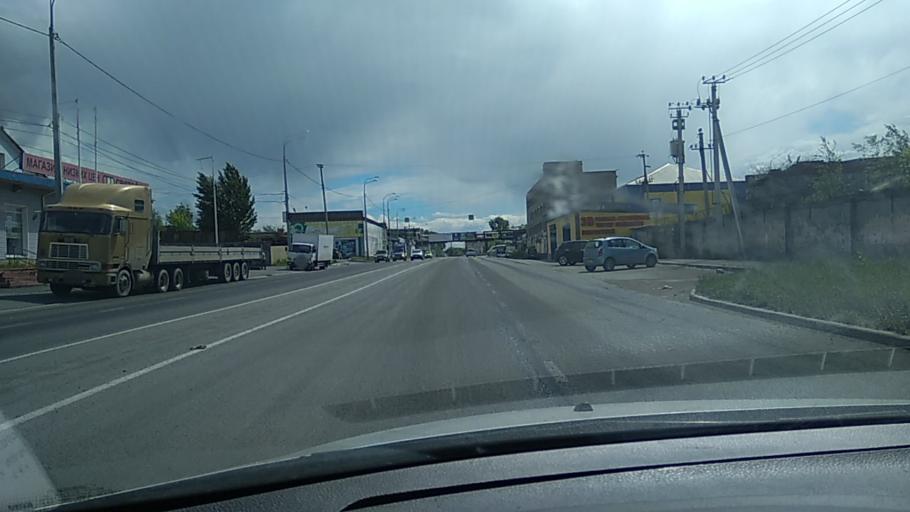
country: RU
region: Sverdlovsk
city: Nizhniy Tagil
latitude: 57.9203
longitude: 59.9888
